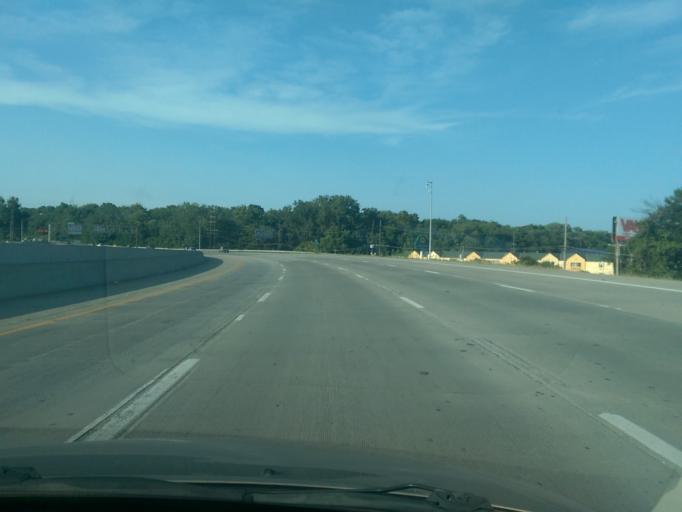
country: US
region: Missouri
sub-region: Clay County
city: North Kansas City
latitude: 39.1458
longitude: -94.5606
